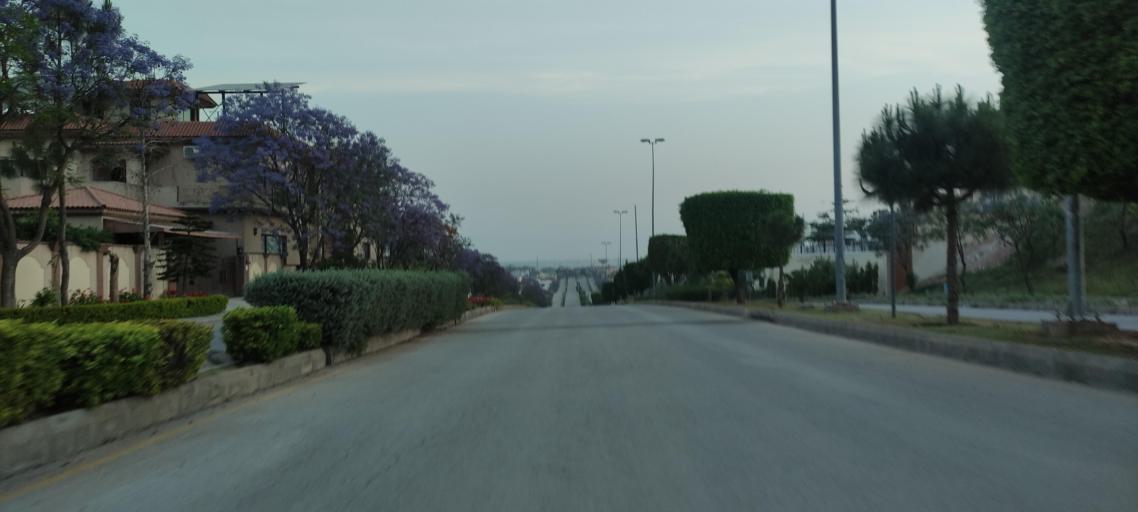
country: PK
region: Punjab
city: Rawalpindi
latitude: 33.5206
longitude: 73.1650
